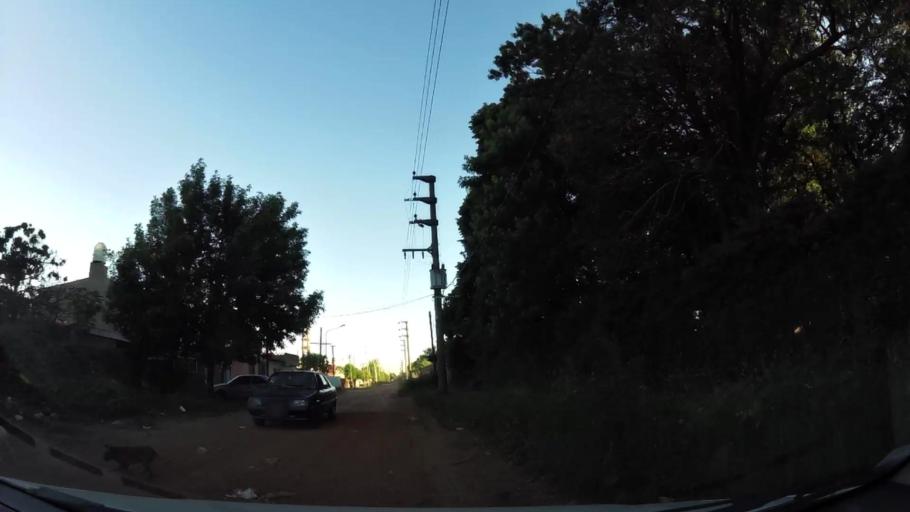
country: AR
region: Buenos Aires
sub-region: Partido de Moron
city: Moron
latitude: -34.7220
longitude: -58.6163
